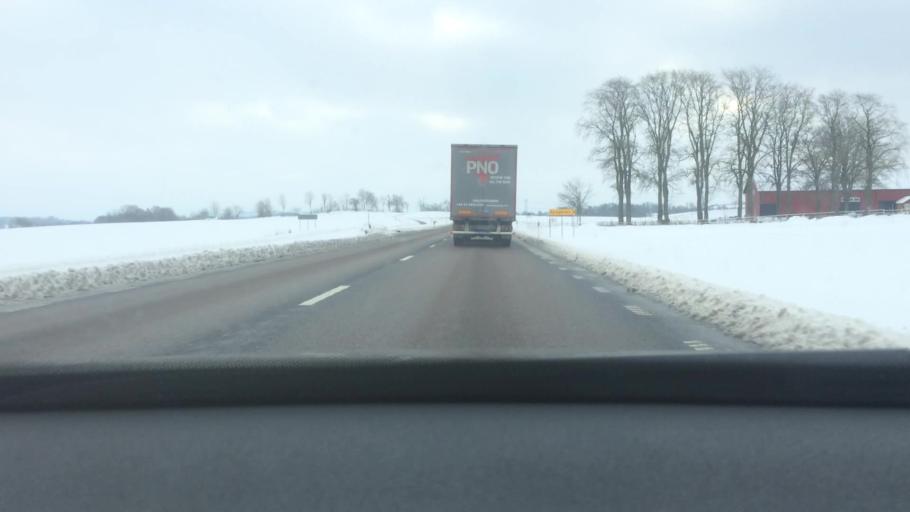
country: SE
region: Vaestra Goetaland
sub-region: Falkopings Kommun
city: Falkoeping
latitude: 58.2040
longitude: 13.5604
